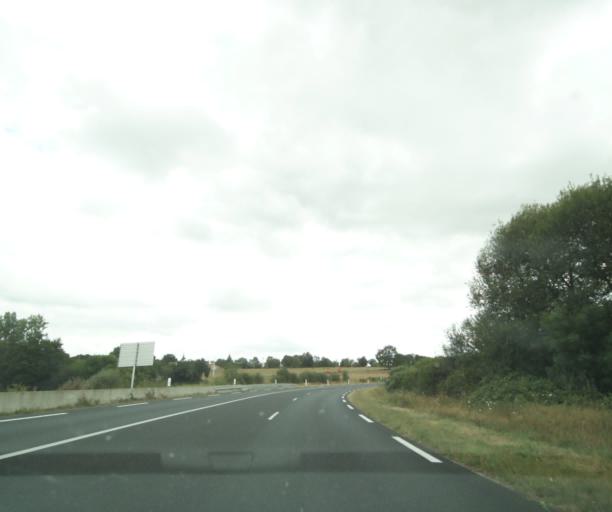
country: FR
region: Pays de la Loire
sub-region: Departement de Maine-et-Loire
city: La Romagne
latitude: 47.0570
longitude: -1.0106
